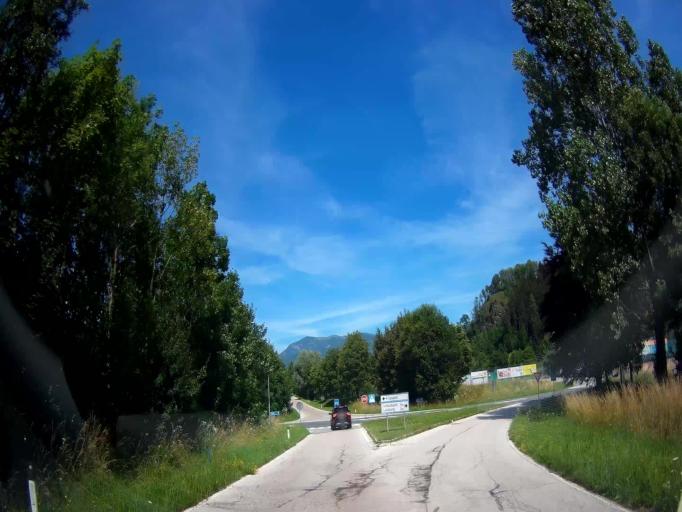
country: AT
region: Carinthia
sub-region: Politischer Bezirk Sankt Veit an der Glan
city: Friesach
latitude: 46.9521
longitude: 14.4191
